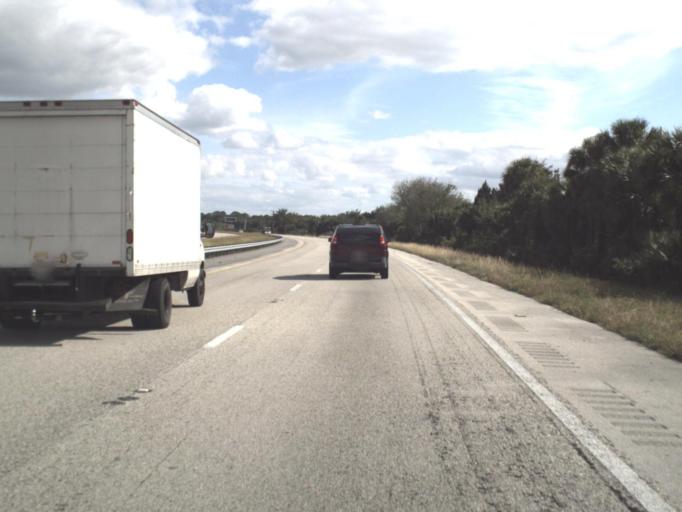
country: US
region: Florida
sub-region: Brevard County
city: Port Saint John
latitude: 28.4157
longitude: -80.8411
